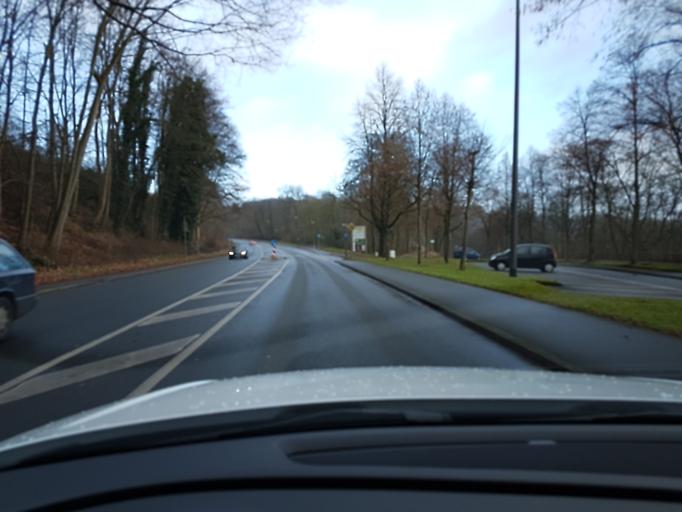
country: DE
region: North Rhine-Westphalia
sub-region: Regierungsbezirk Dusseldorf
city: Essen
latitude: 51.4049
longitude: 7.0115
